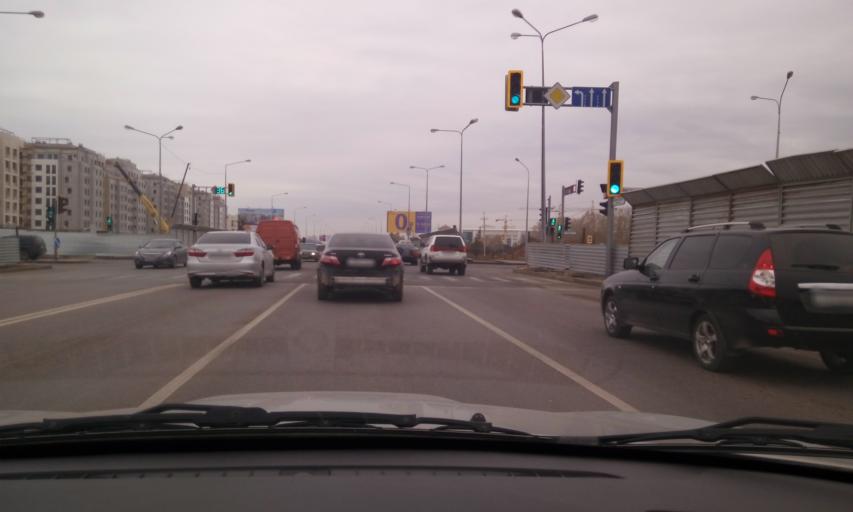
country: KZ
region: Astana Qalasy
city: Astana
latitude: 51.0990
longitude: 71.4061
